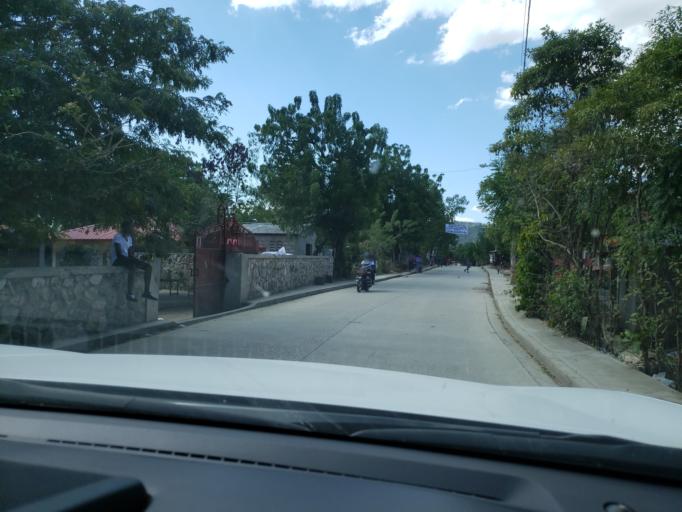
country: HT
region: Grandans
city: Anse-a-Veau
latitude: 18.4508
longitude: -73.3812
